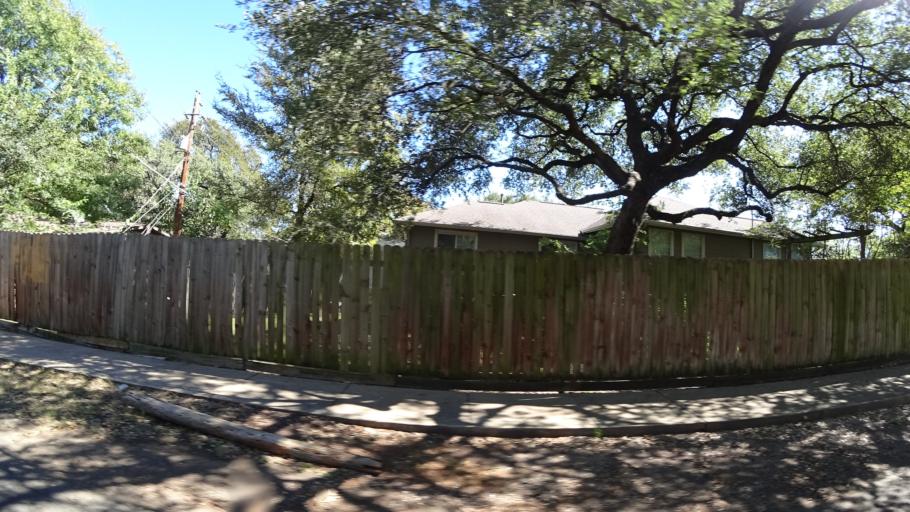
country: US
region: Texas
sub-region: Travis County
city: Rollingwood
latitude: 30.2349
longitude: -97.7797
